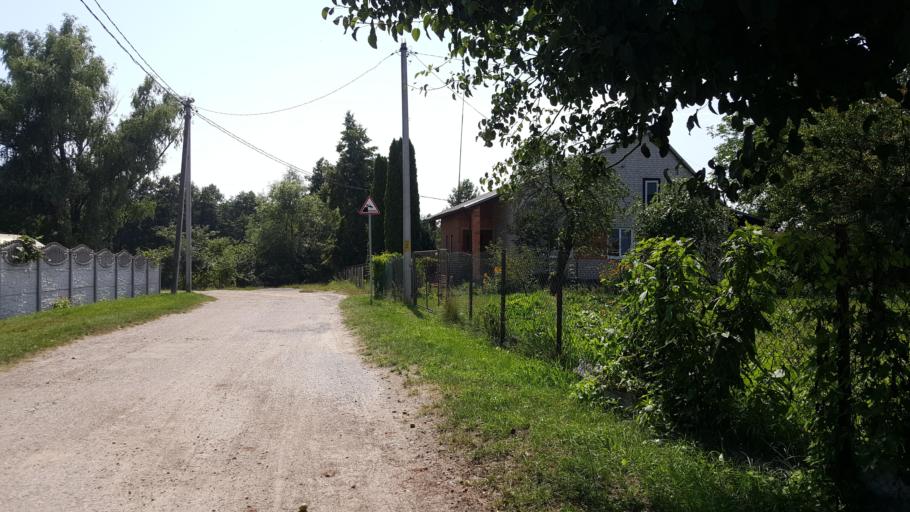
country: BY
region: Brest
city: Zhabinka
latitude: 52.1878
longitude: 24.0238
